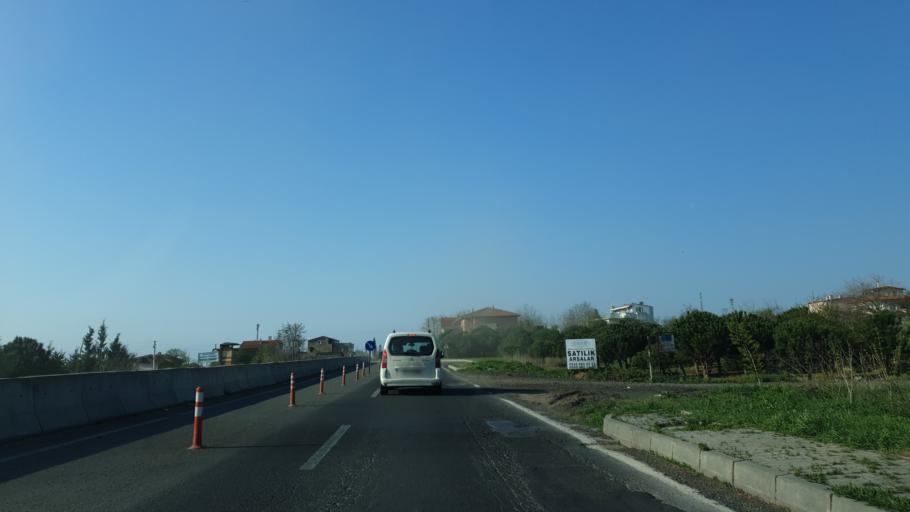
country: TR
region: Tekirdag
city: Corlu
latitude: 41.0167
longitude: 27.7200
